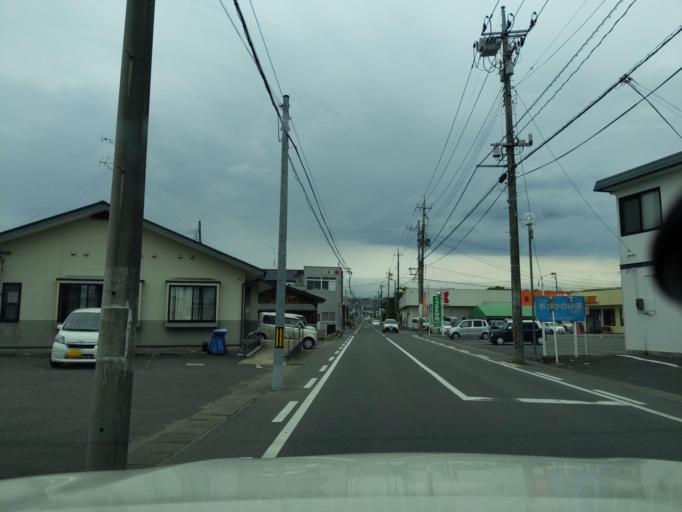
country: JP
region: Fukushima
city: Koriyama
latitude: 37.3561
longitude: 140.3618
